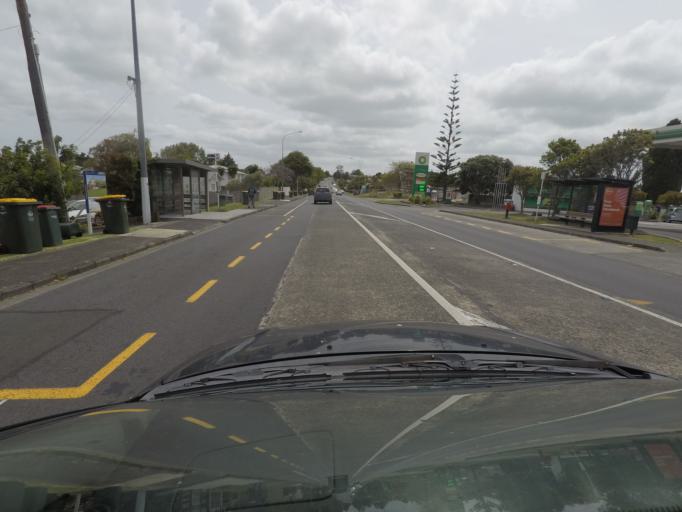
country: NZ
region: Auckland
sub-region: Auckland
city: Pakuranga
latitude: -36.8963
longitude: 174.9219
